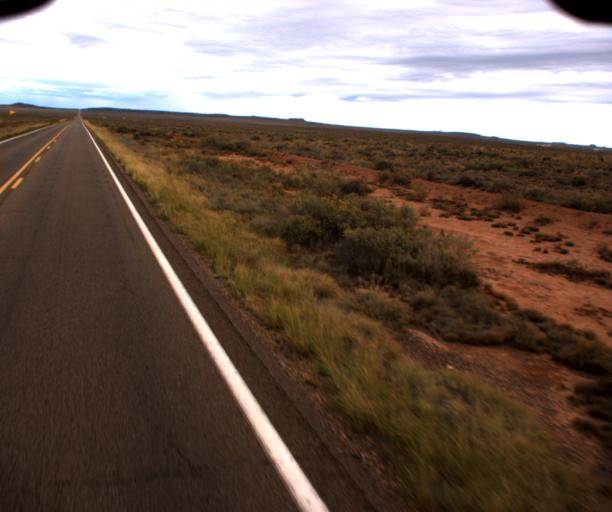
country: US
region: Arizona
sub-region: Navajo County
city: Holbrook
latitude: 34.7465
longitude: -110.1210
